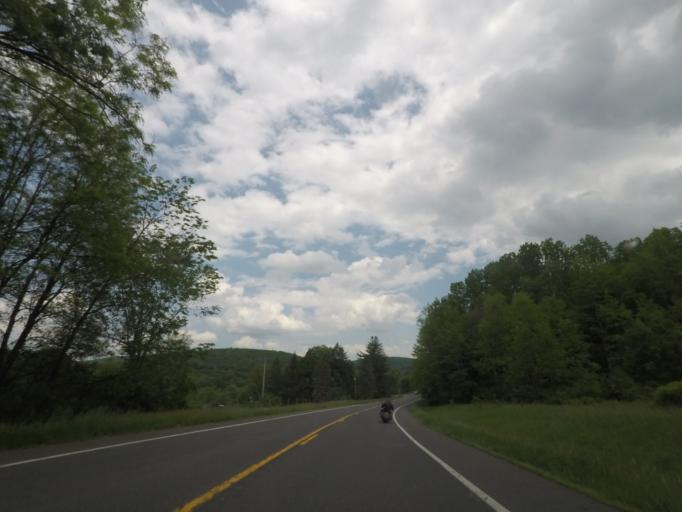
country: US
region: New York
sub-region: Dutchess County
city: Pine Plains
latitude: 42.0886
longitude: -73.6811
